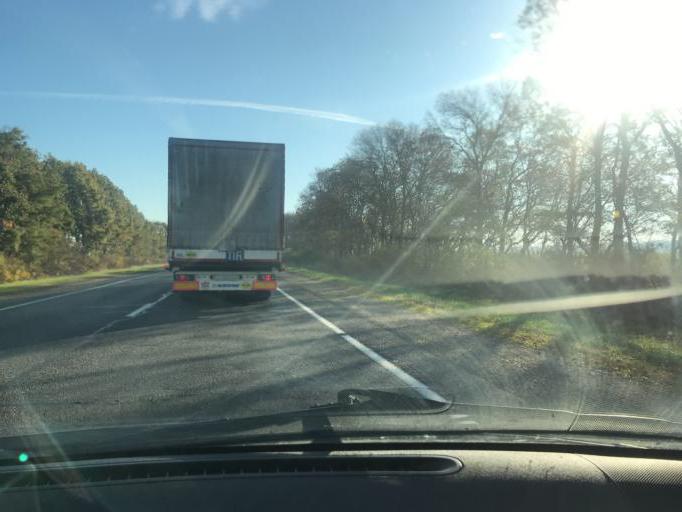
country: BY
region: Brest
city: Ivanava
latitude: 52.1468
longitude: 25.4478
